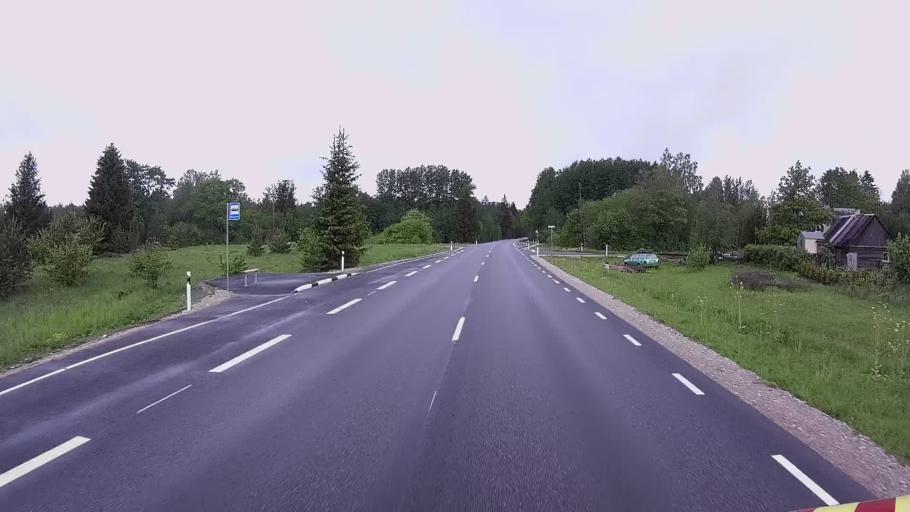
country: EE
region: Raplamaa
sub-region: Maerjamaa vald
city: Marjamaa
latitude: 58.9248
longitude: 24.3977
